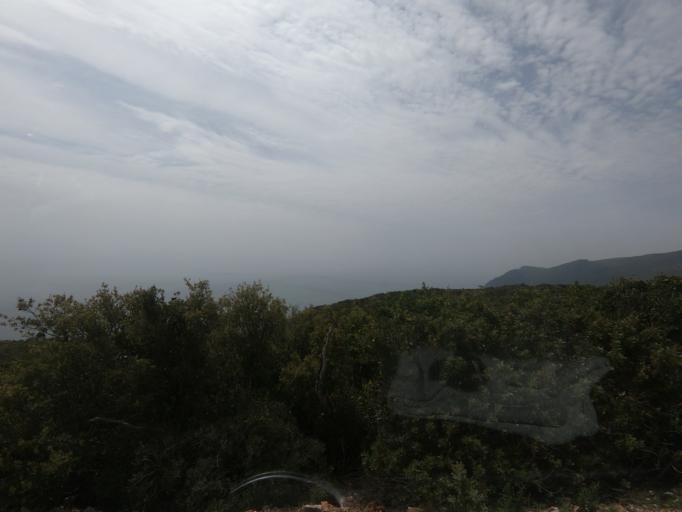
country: PT
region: Setubal
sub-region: Setubal
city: Setubal
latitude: 38.4909
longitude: -8.9582
